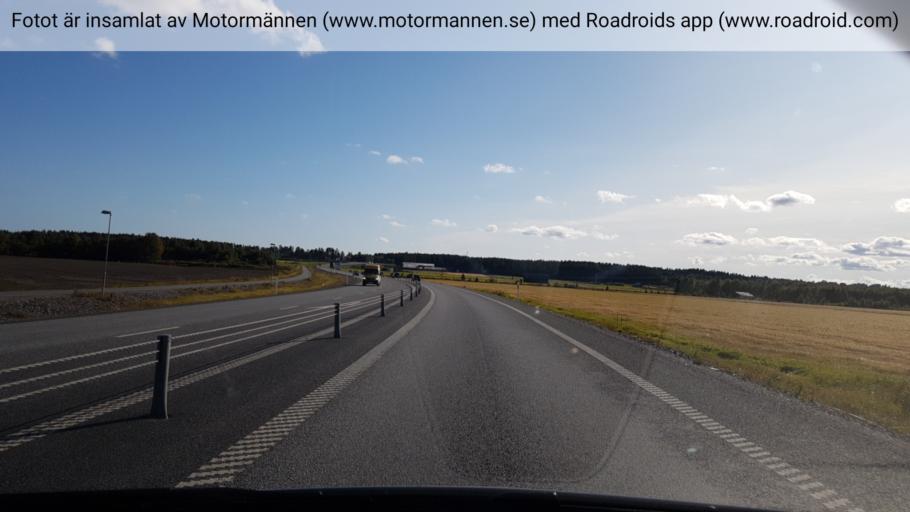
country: SE
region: Vaesterbotten
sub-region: Umea Kommun
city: Roback
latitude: 63.8530
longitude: 20.1929
